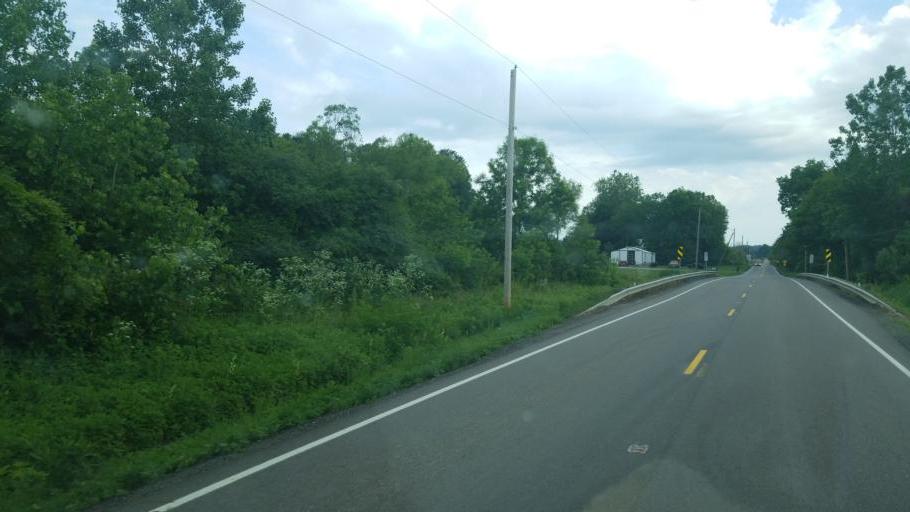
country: US
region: Ohio
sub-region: Knox County
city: Danville
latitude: 40.5051
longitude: -82.2868
